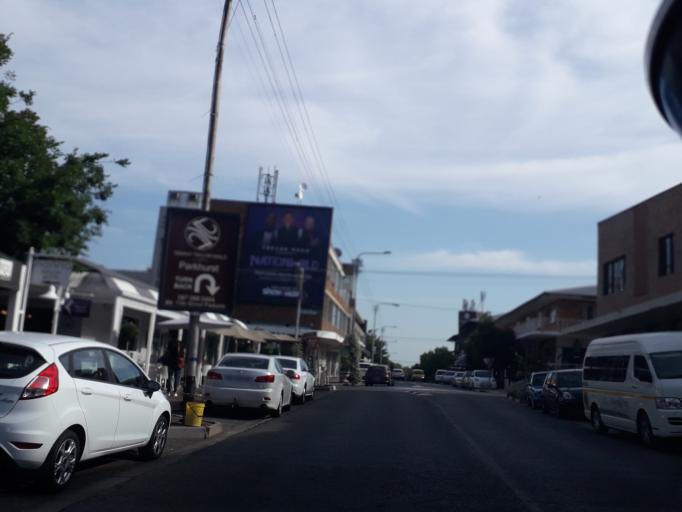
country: ZA
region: Gauteng
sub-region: City of Johannesburg Metropolitan Municipality
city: Johannesburg
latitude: -26.1394
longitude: 28.0175
